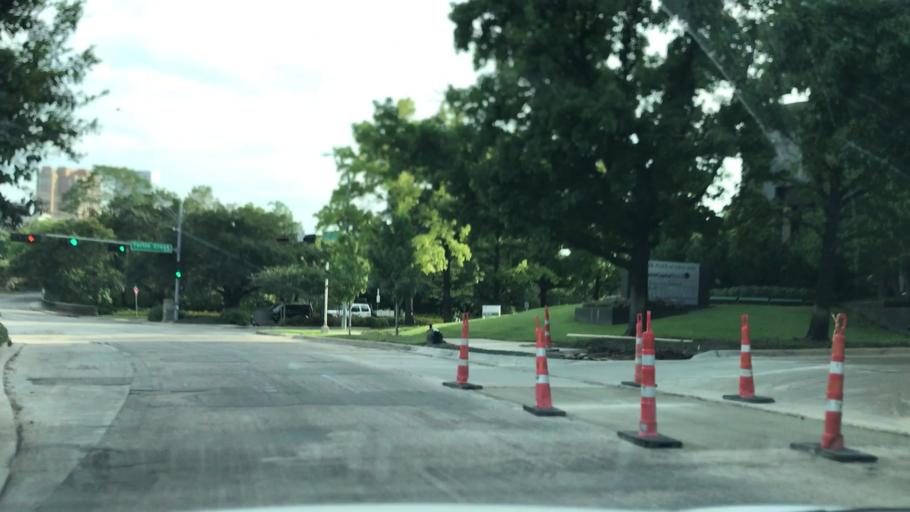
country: US
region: Texas
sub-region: Dallas County
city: Dallas
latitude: 32.8042
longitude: -96.8053
